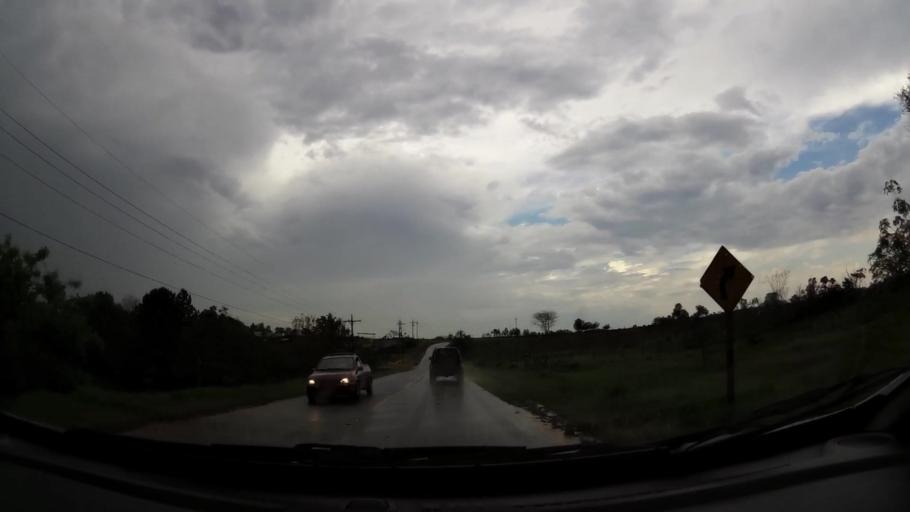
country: PY
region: Alto Parana
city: Presidente Franco
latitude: -25.5818
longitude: -54.6706
